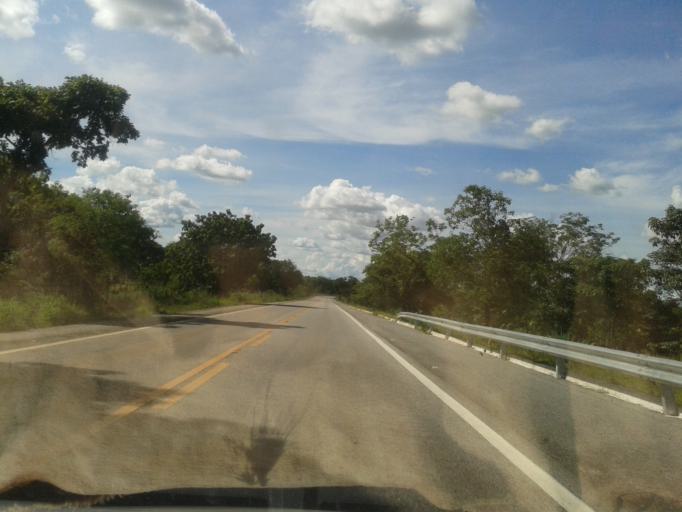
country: BR
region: Goias
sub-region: Mozarlandia
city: Mozarlandia
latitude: -15.1261
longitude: -50.6002
